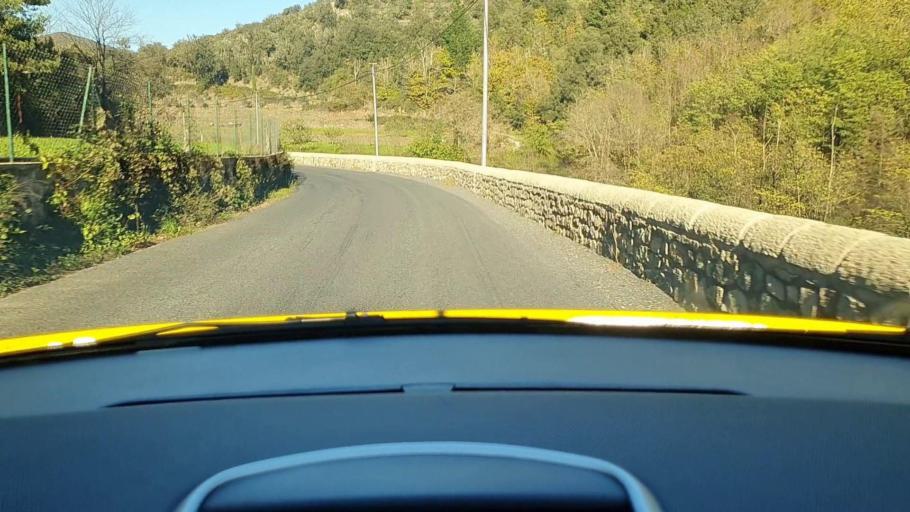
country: FR
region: Languedoc-Roussillon
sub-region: Departement du Gard
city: Sumene
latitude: 43.9911
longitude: 3.7134
